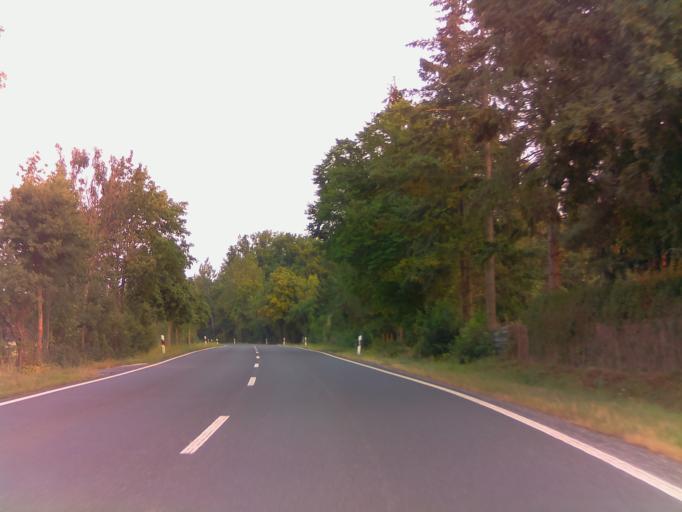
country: DE
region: Thuringia
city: Troistedt
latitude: 50.9305
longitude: 11.2473
